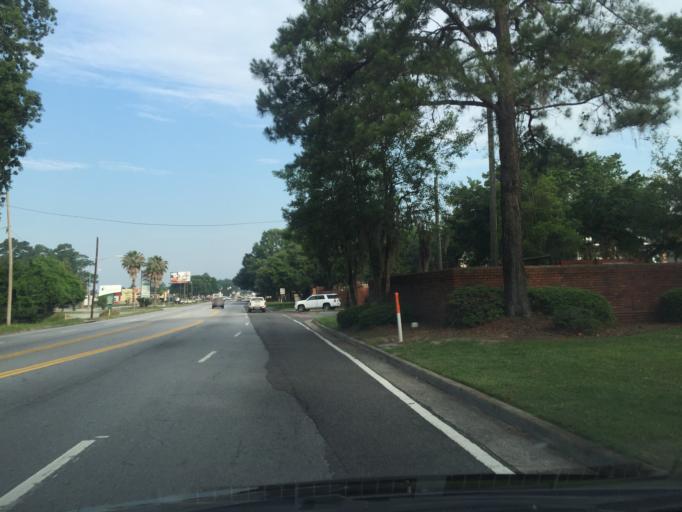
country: US
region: Georgia
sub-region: Chatham County
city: Isle of Hope
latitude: 32.0080
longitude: -81.1061
